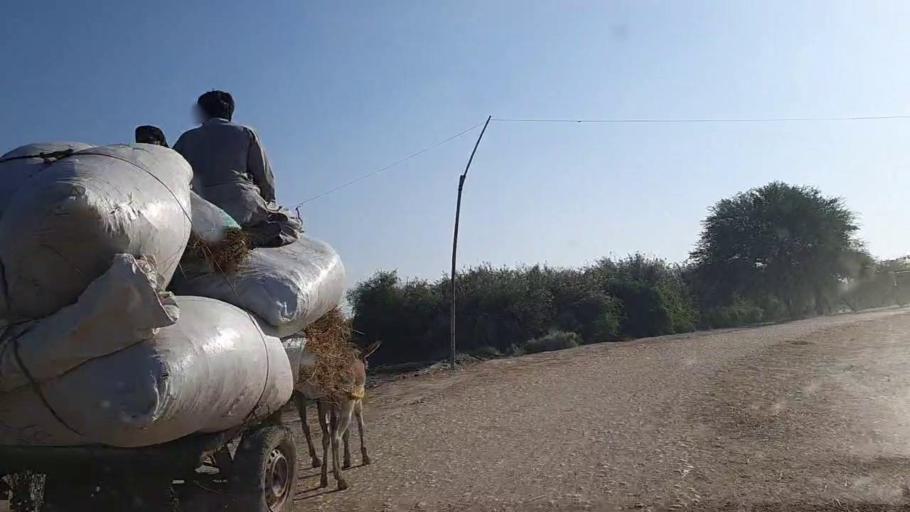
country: PK
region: Sindh
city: Daro Mehar
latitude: 24.6243
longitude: 68.0811
